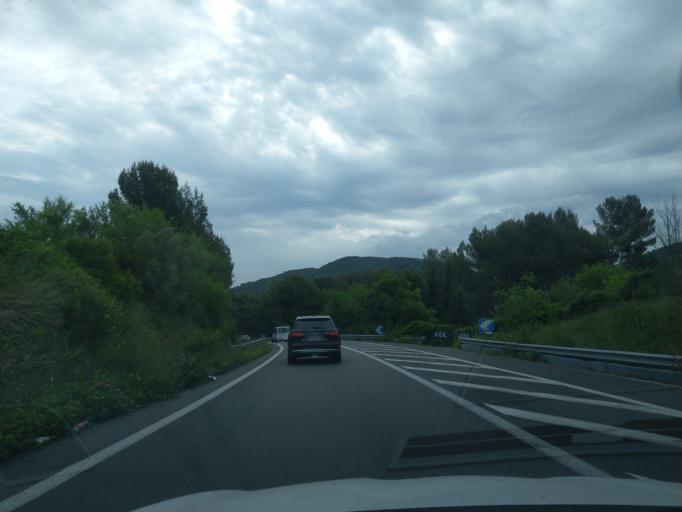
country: FR
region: Provence-Alpes-Cote d'Azur
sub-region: Departement des Bouches-du-Rhone
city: Aubagne
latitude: 43.2829
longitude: 5.5761
